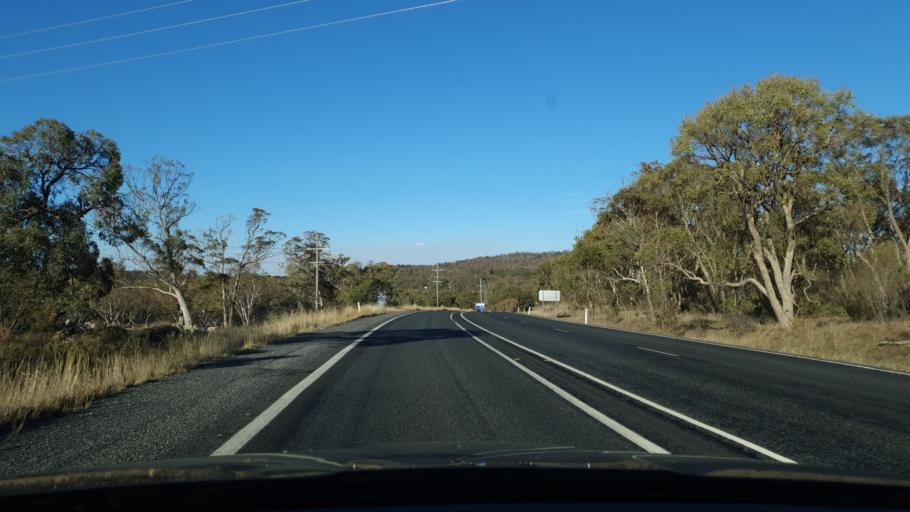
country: AU
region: Queensland
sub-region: Southern Downs
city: Stanthorpe
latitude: -28.6856
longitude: 151.9132
